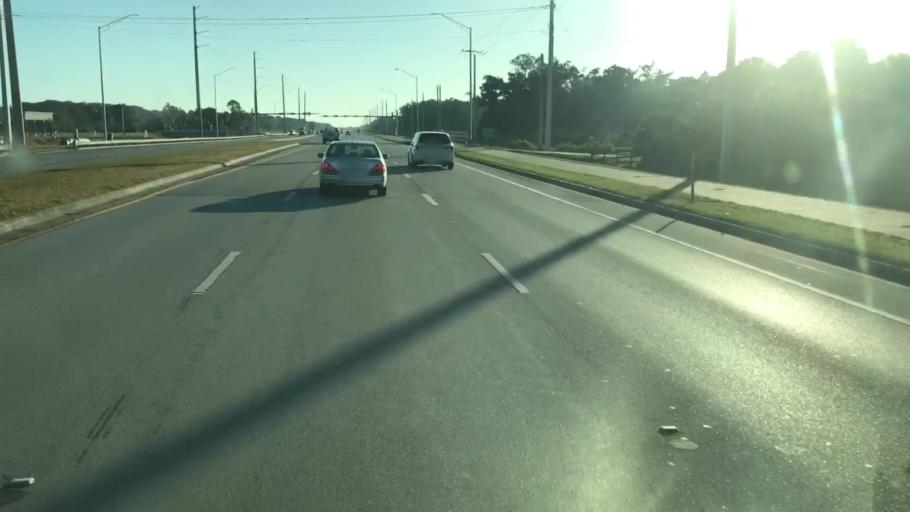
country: US
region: Florida
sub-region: Collier County
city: Orangetree
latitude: 26.2752
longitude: -81.6265
